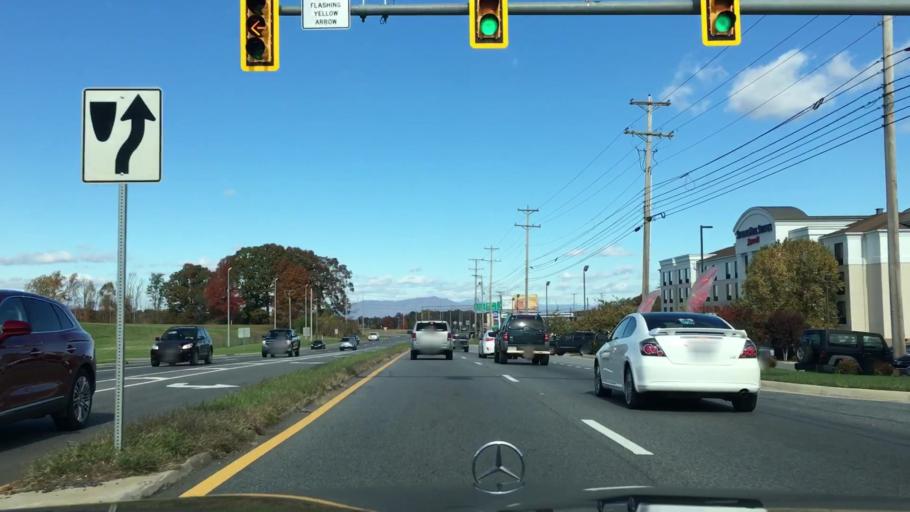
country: US
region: Virginia
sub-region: Campbell County
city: Timberlake
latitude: 37.3341
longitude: -79.1916
